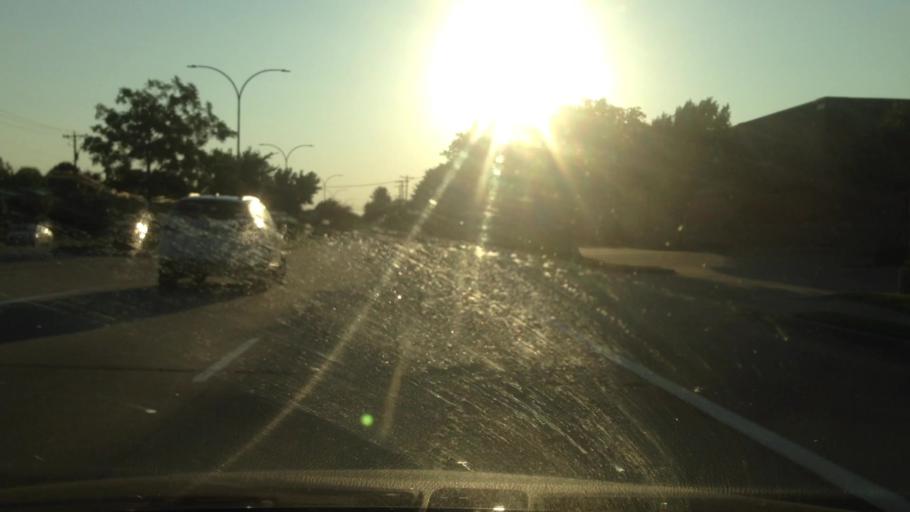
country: US
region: Texas
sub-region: Tarrant County
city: Dalworthington Gardens
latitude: 32.6488
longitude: -97.1362
